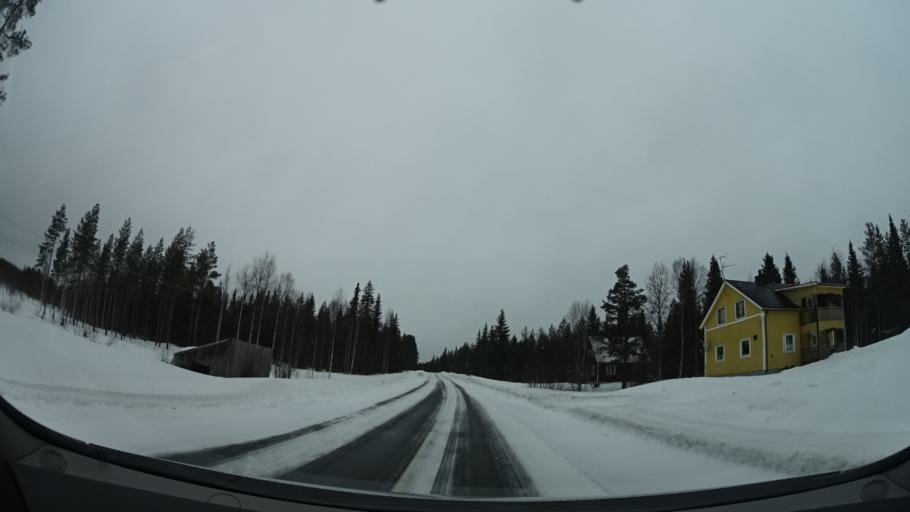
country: SE
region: Vaesterbotten
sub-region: Mala Kommun
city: Mala
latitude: 65.0826
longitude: 18.9942
